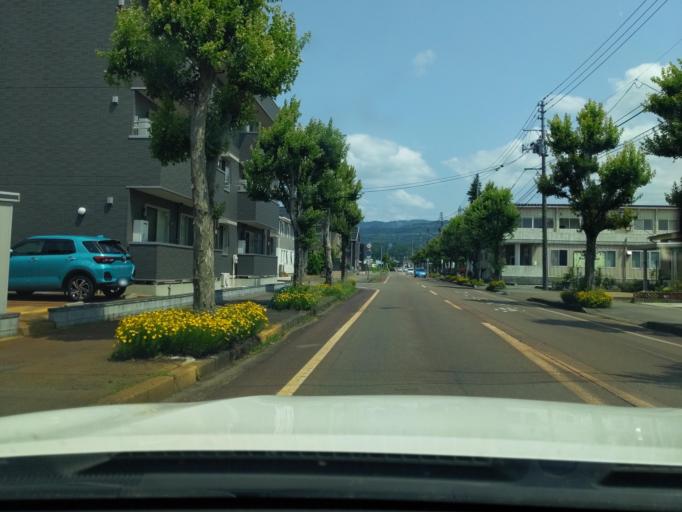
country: JP
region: Niigata
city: Nagaoka
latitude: 37.4290
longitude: 138.8567
